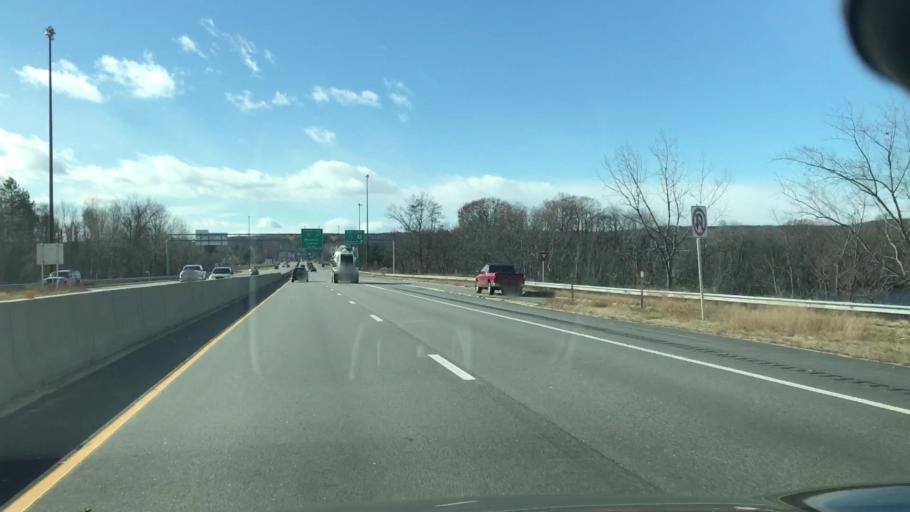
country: US
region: New Hampshire
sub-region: Merrimack County
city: Concord
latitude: 43.2186
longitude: -71.5266
